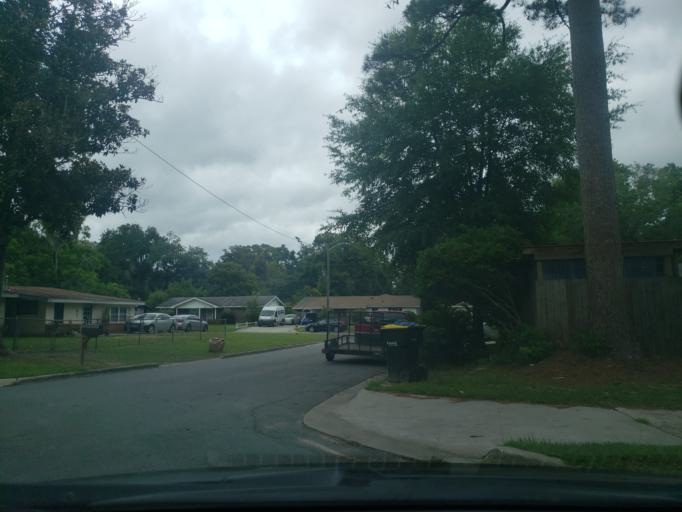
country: US
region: Georgia
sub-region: Chatham County
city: Montgomery
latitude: 31.9914
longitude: -81.1160
